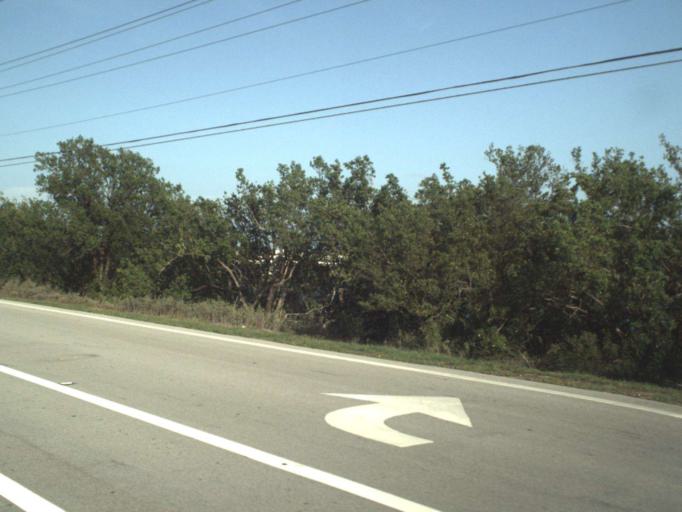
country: US
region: Florida
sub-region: Monroe County
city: Marathon
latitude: 24.7795
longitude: -80.9165
